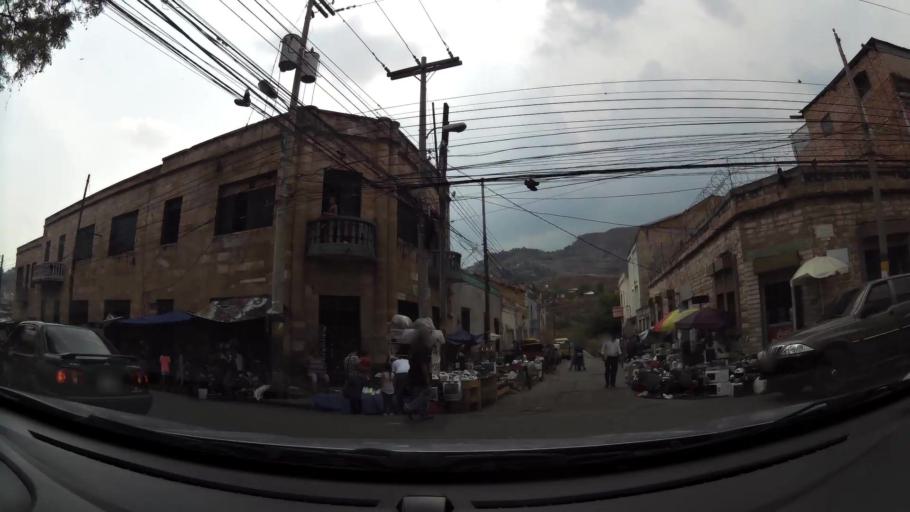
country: HN
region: Francisco Morazan
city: Tegucigalpa
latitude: 14.1059
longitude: -87.2094
